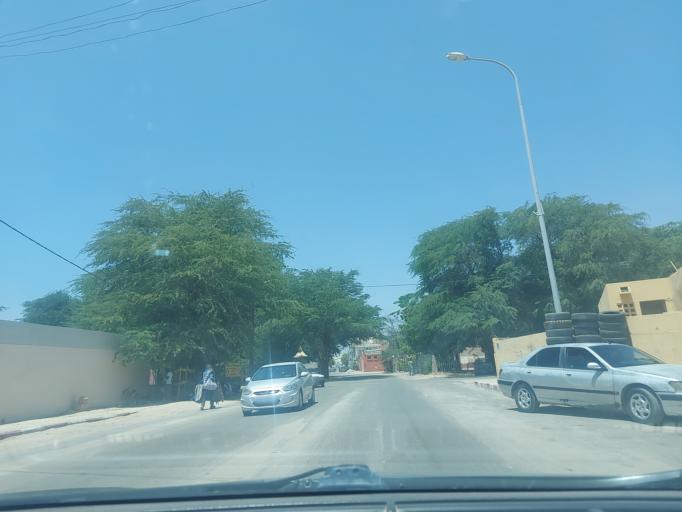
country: MR
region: Nouakchott
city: Nouakchott
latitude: 18.0889
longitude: -15.9820
